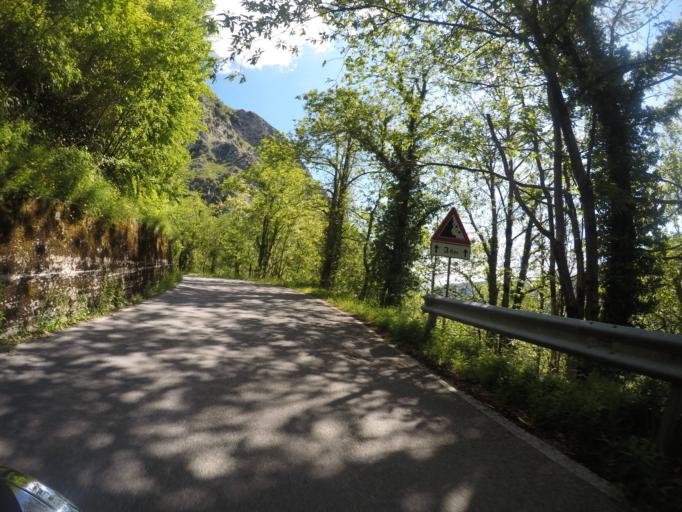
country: IT
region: Tuscany
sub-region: Provincia di Lucca
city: Careggine
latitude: 44.0709
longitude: 10.3184
